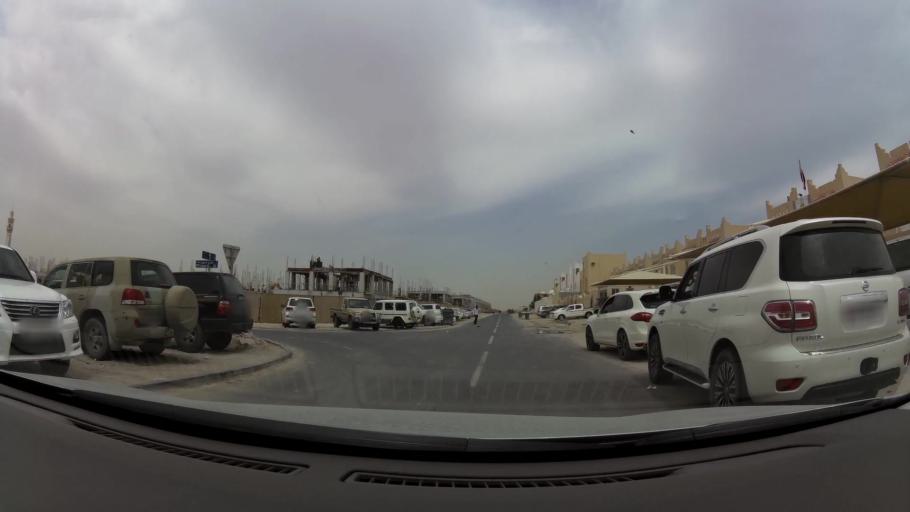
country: QA
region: Baladiyat ar Rayyan
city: Ar Rayyan
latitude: 25.2914
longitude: 51.4558
